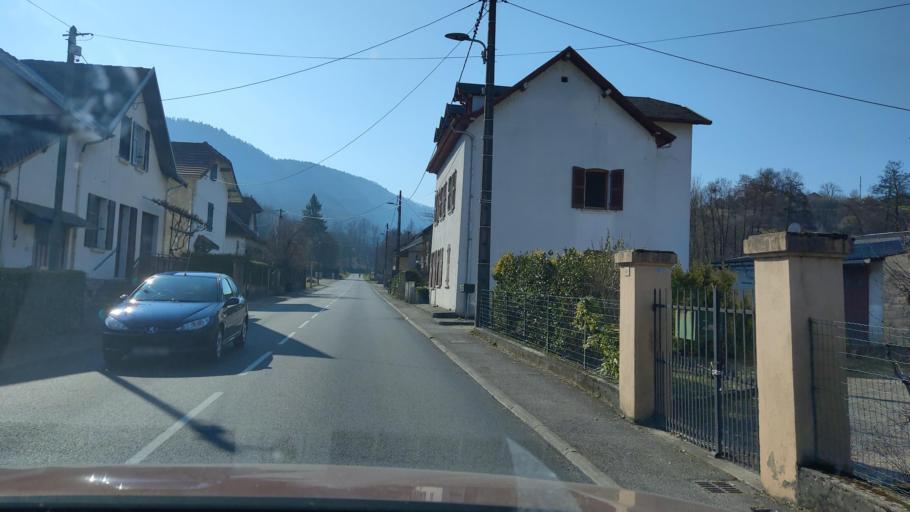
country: FR
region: Rhone-Alpes
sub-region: Departement de la Savoie
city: La Bridoire
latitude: 45.5246
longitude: 5.7389
